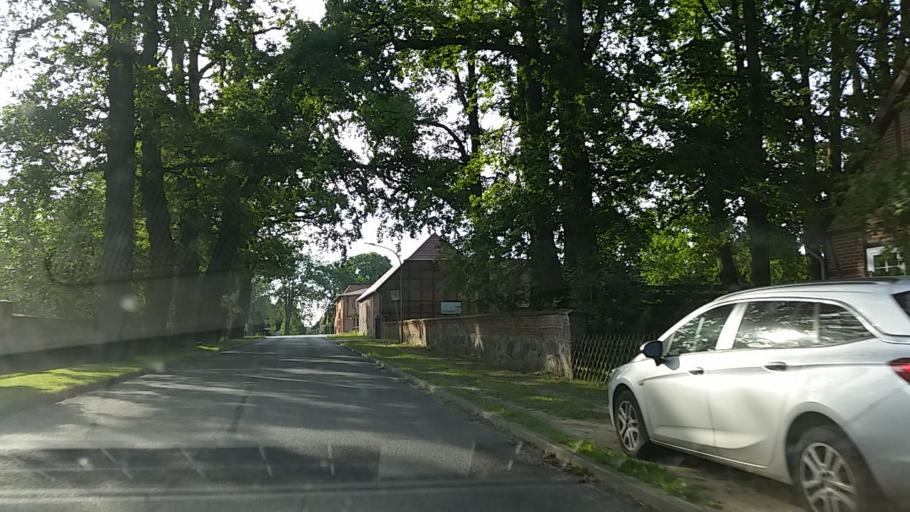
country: DE
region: Lower Saxony
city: Wieren
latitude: 52.9096
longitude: 10.6655
